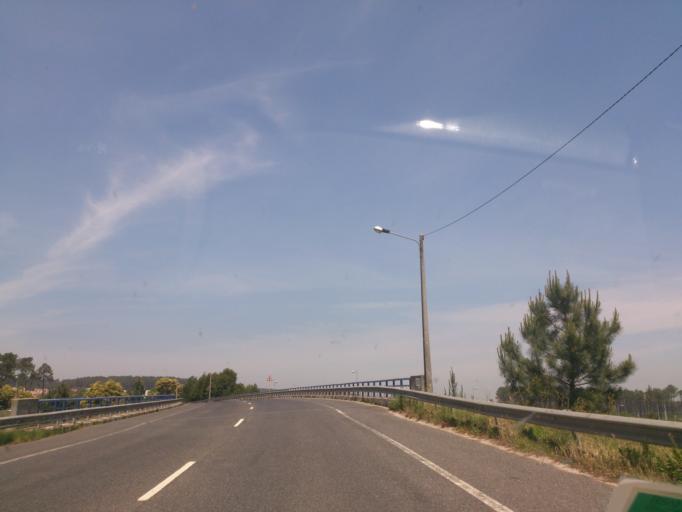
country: PT
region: Leiria
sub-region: Alcobaca
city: Alcobaca
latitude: 39.5846
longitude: -9.0126
